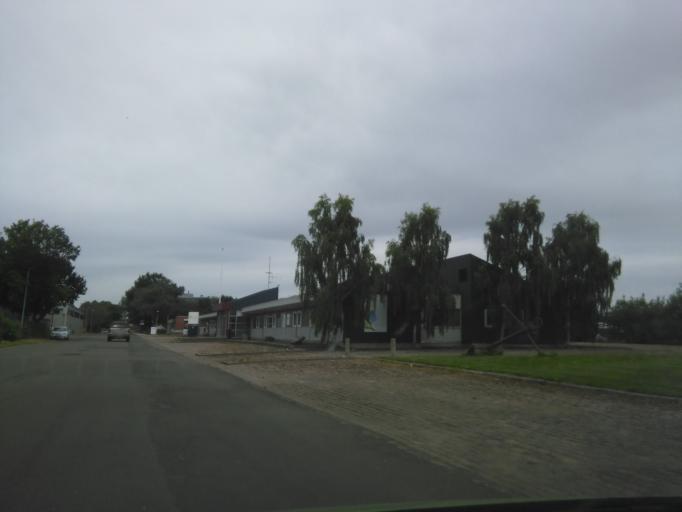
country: DK
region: Central Jutland
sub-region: Horsens Kommune
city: Horsens
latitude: 55.8581
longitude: 9.8714
